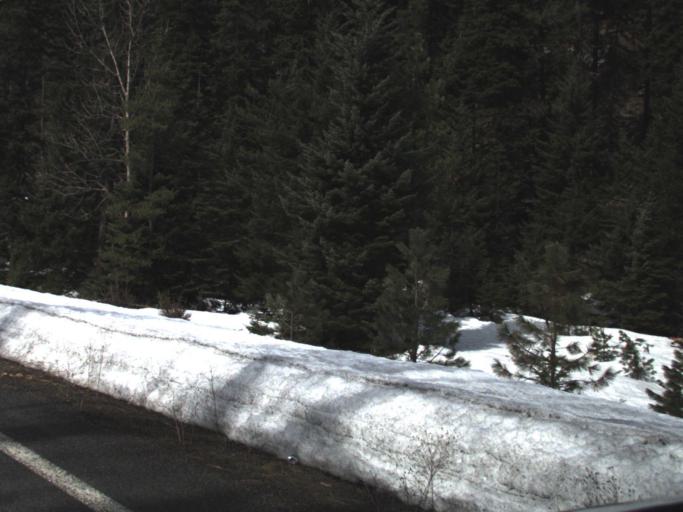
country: US
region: Washington
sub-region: Kittitas County
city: Cle Elum
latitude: 46.9677
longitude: -121.2158
